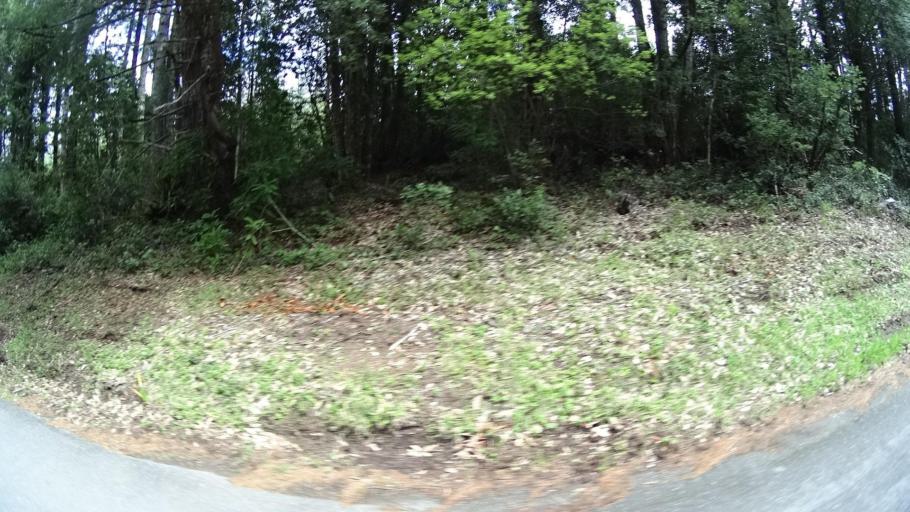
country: US
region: California
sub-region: Humboldt County
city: Blue Lake
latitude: 40.8032
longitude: -123.9856
